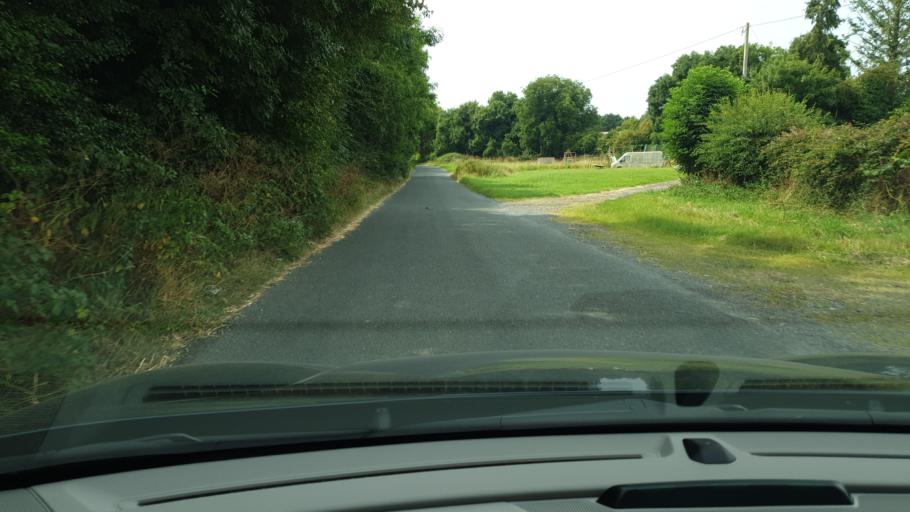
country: IE
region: Leinster
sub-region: An Mhi
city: Athboy
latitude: 53.6605
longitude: -6.9386
